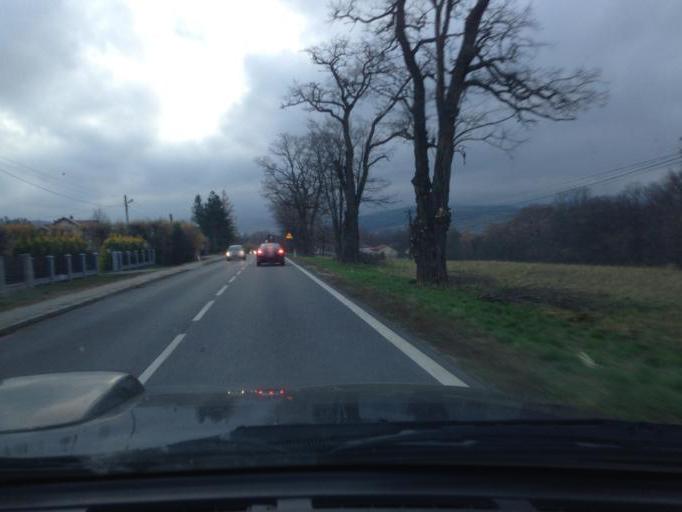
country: PL
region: Subcarpathian Voivodeship
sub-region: Powiat jasielski
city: Nowy Zmigrod
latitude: 49.6159
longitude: 21.5355
